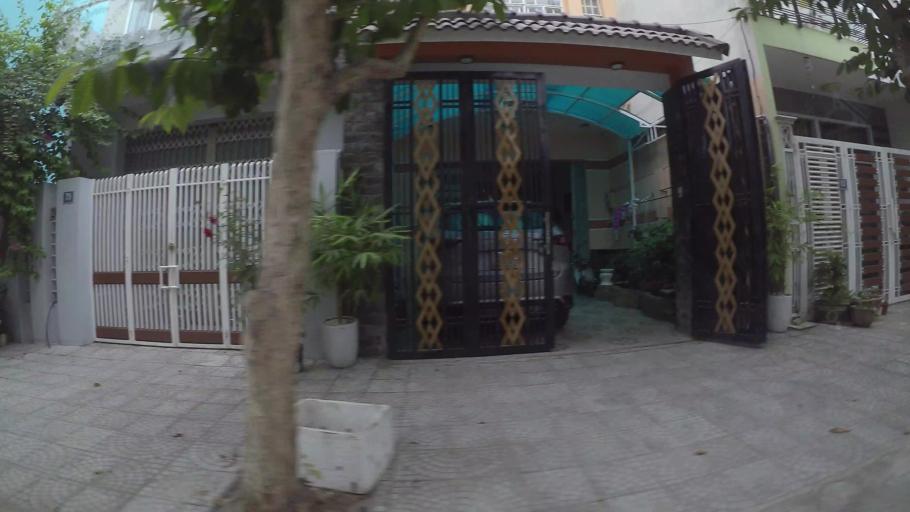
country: VN
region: Da Nang
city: Thanh Khe
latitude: 16.0548
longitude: 108.1847
